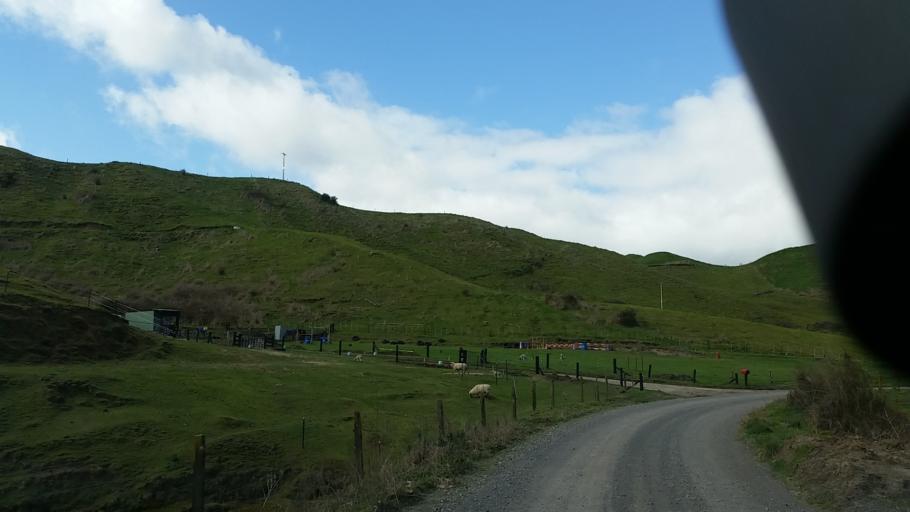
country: NZ
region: Waikato
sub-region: South Waikato District
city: Tokoroa
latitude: -38.3681
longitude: 176.0891
